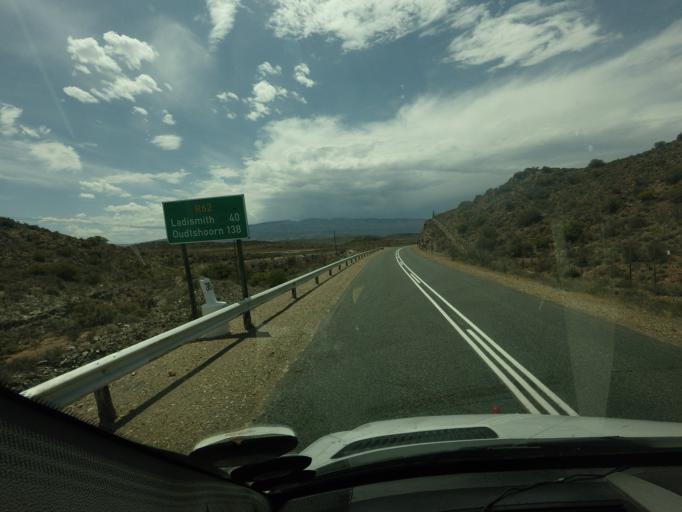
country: ZA
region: Western Cape
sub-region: Eden District Municipality
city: Ladismith
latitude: -33.6967
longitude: 20.9642
